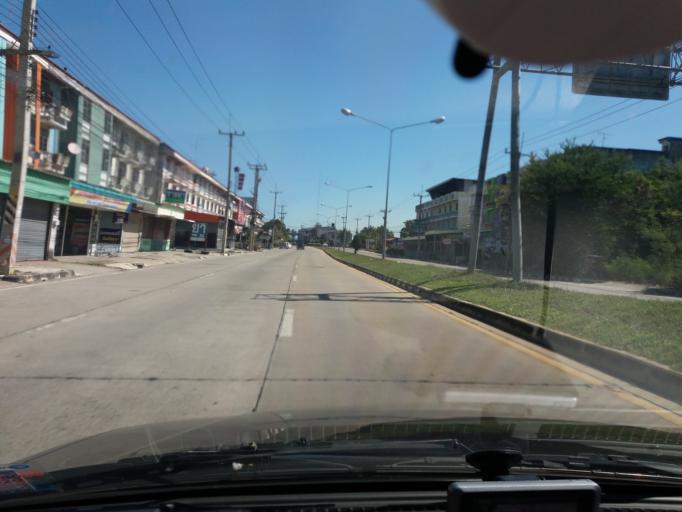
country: TH
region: Suphan Buri
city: Suphan Buri
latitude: 14.4622
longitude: 100.1475
